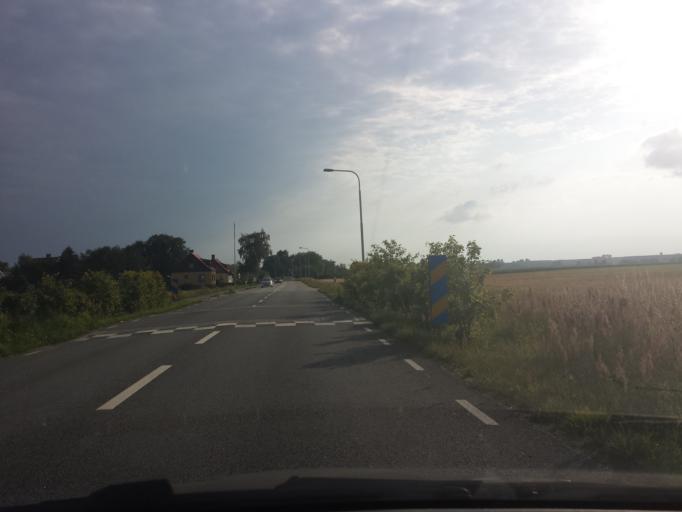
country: SE
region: Skane
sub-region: Ystads Kommun
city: Kopingebro
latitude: 55.4488
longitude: 14.0181
